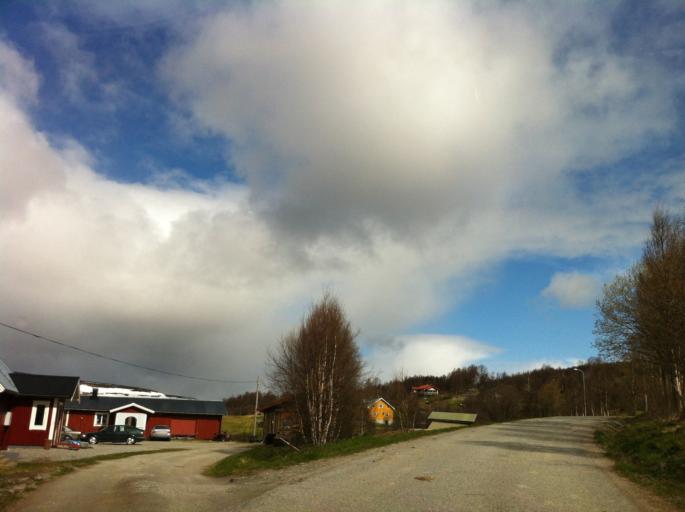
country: NO
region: Sor-Trondelag
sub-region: Tydal
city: Aas
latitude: 62.6336
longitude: 12.4447
